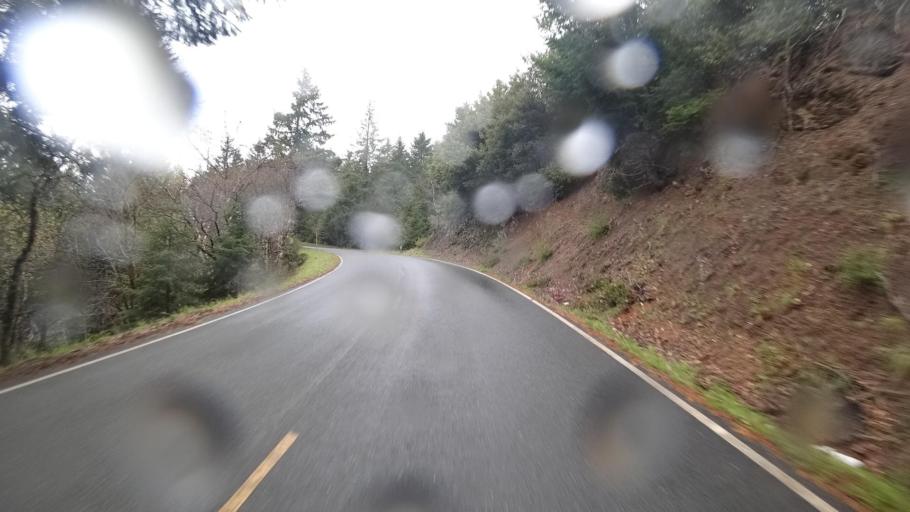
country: US
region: California
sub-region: Humboldt County
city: Westhaven-Moonstone
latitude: 41.1440
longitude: -123.8496
